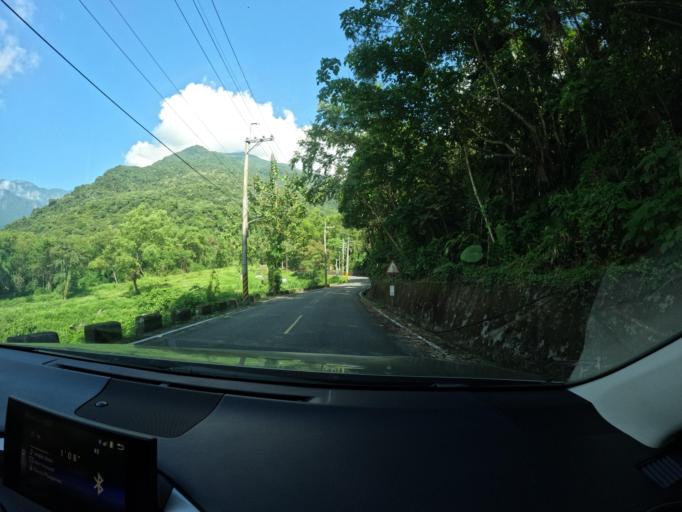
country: TW
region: Taiwan
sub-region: Hualien
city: Hualian
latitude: 23.5879
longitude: 121.3567
